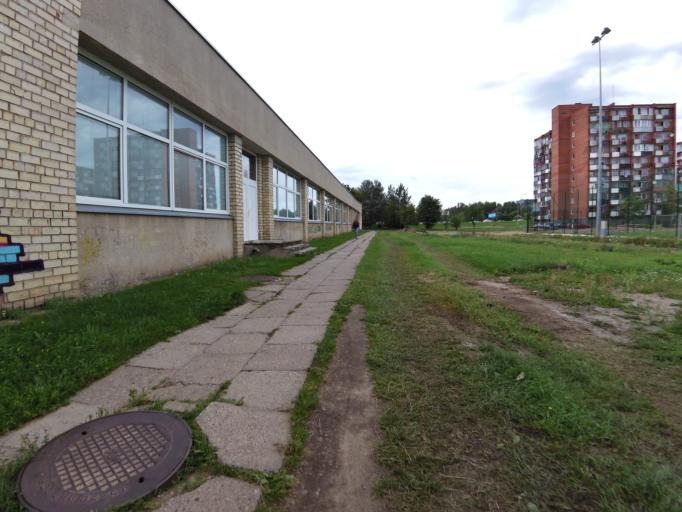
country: LT
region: Vilnius County
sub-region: Vilnius
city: Vilnius
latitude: 54.7120
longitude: 25.2794
